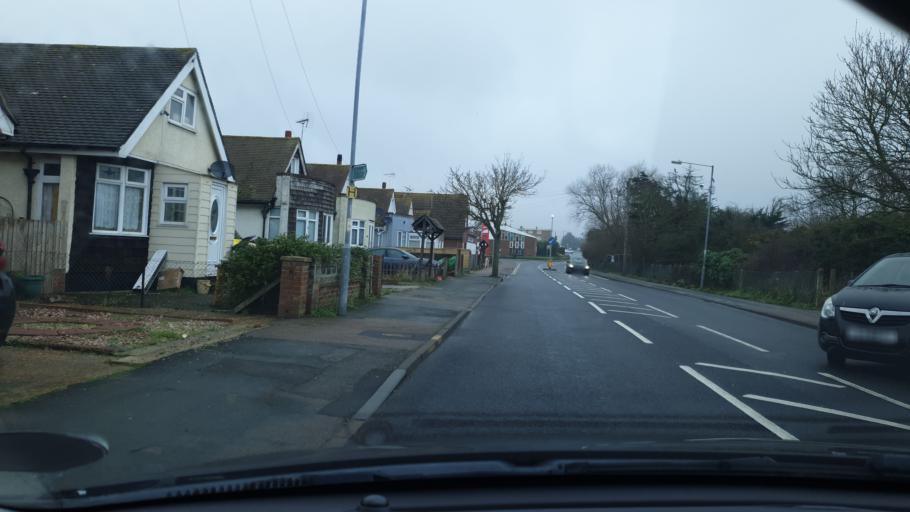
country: GB
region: England
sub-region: Essex
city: Clacton-on-Sea
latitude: 51.7802
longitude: 1.1203
